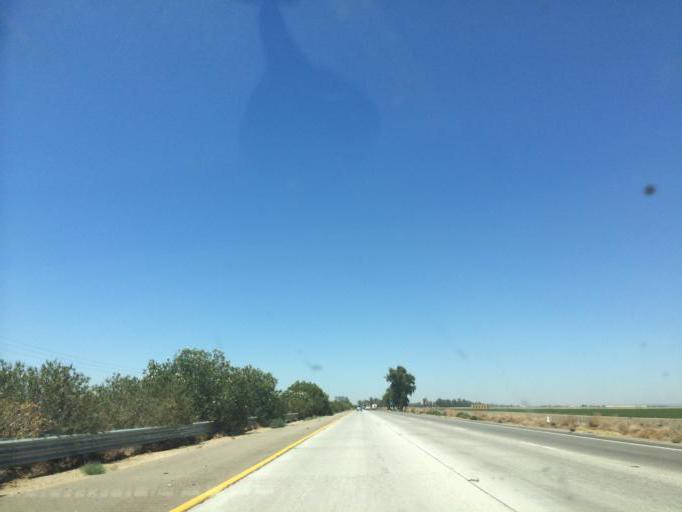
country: US
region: California
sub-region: Kern County
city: Greenfield
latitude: 35.1584
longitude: -118.9997
